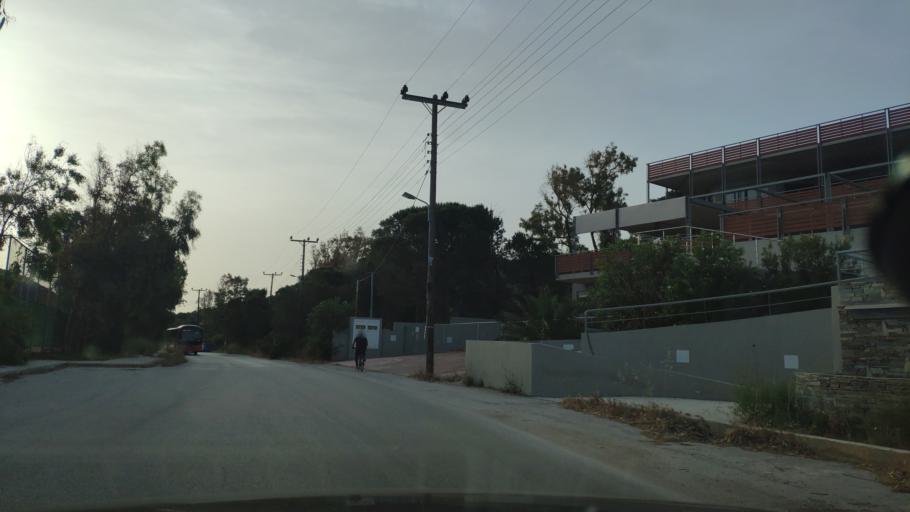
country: GR
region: Attica
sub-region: Nomarchia Anatolikis Attikis
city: Limin Mesoyaias
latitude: 37.8674
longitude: 24.0327
